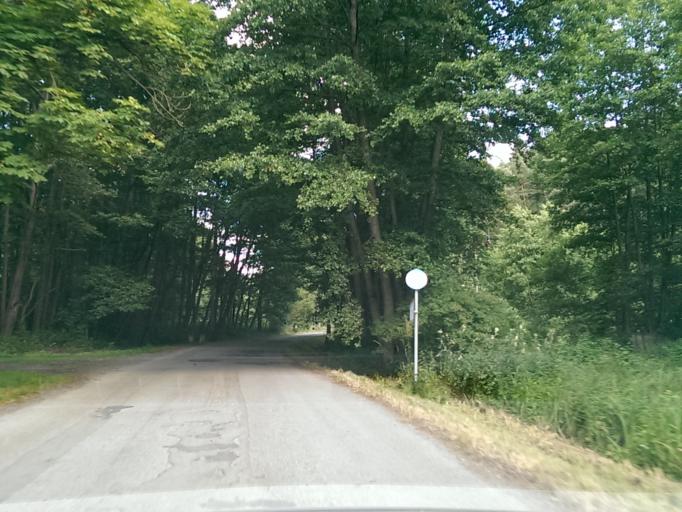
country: CZ
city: Duba
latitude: 50.5307
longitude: 14.5630
